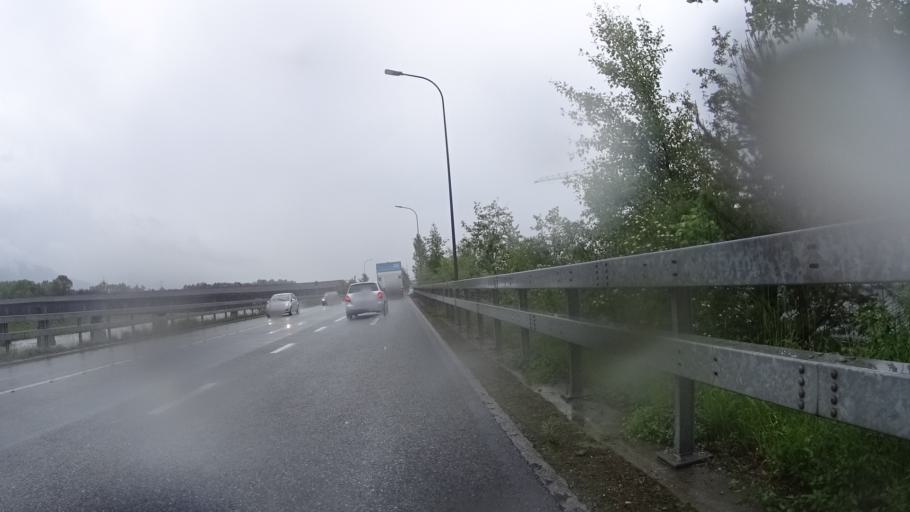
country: LI
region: Vaduz
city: Vaduz
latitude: 47.1315
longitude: 9.5132
